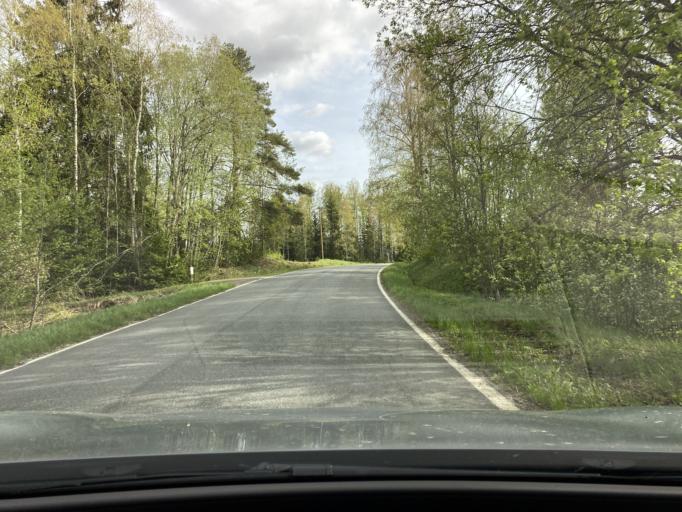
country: FI
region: Varsinais-Suomi
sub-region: Salo
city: Kiikala
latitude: 60.5231
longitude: 23.5426
